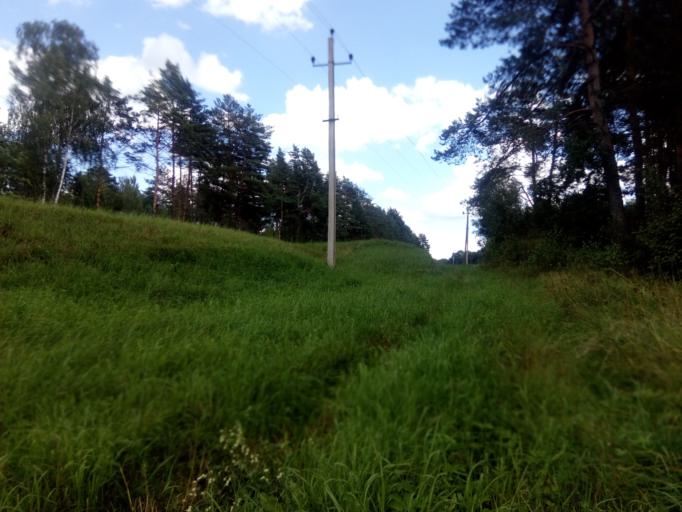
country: BY
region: Vitebsk
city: Dzisna
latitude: 55.6812
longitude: 28.2856
